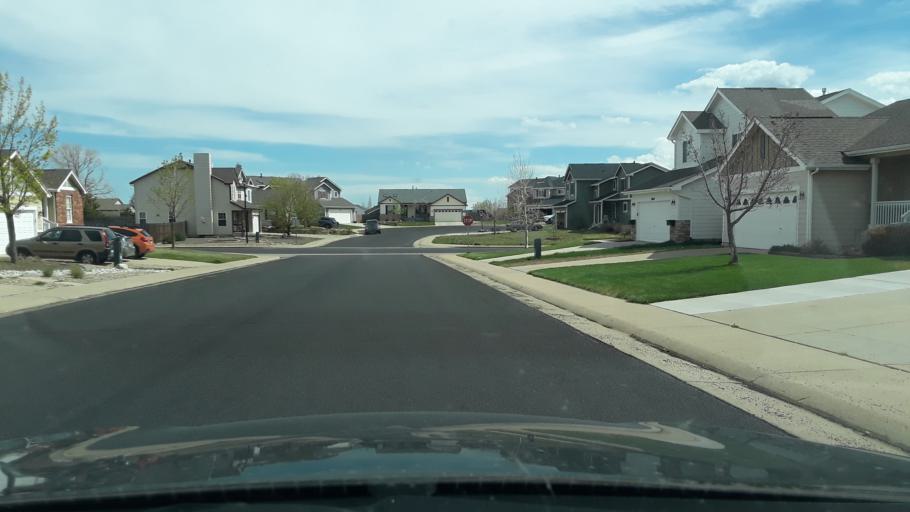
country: US
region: Colorado
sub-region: El Paso County
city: Monument
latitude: 39.0807
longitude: -104.8684
